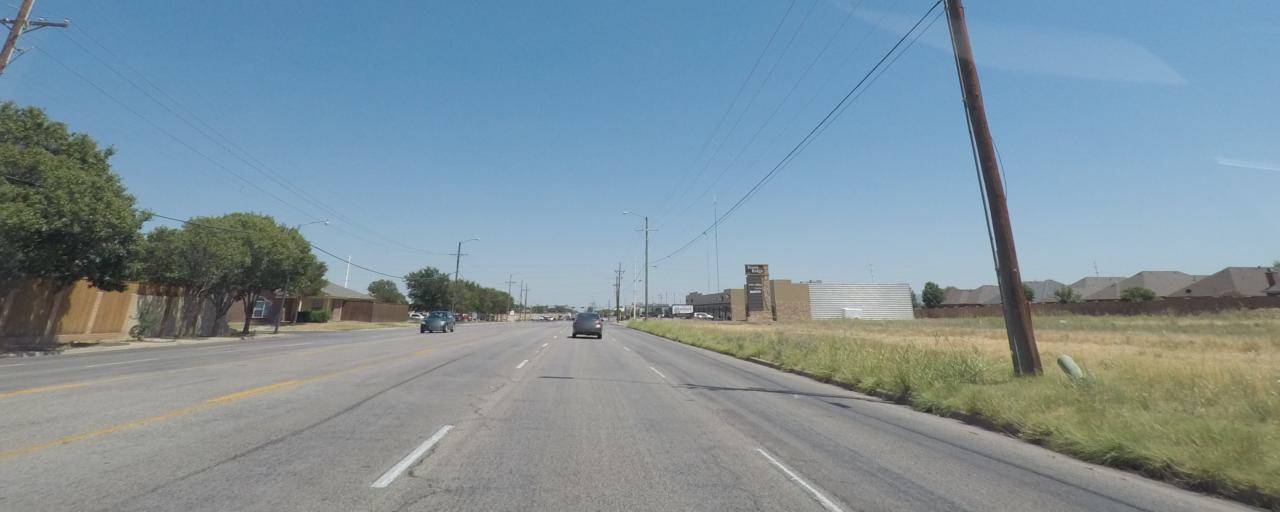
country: US
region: Texas
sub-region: Lubbock County
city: Lubbock
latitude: 33.5052
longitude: -101.8911
